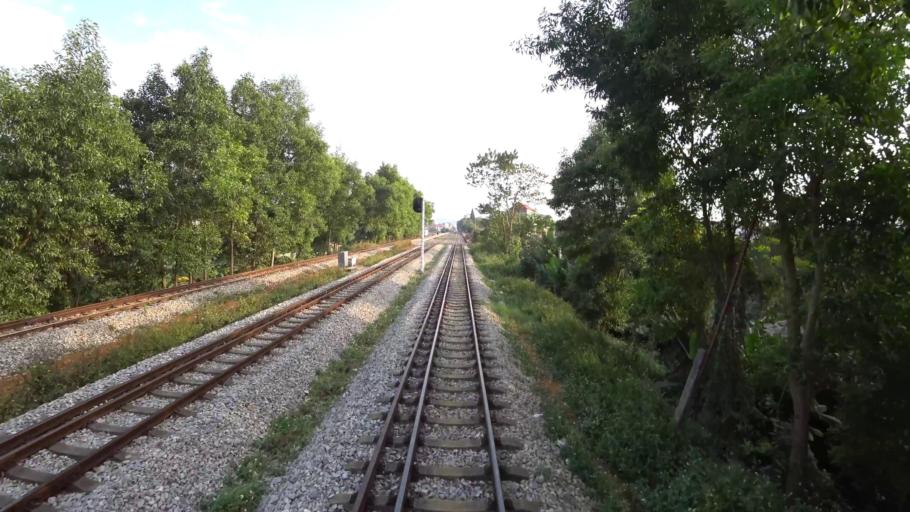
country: VN
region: Lang Son
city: Thi Tran Cao Loc
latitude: 21.8696
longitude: 106.7612
